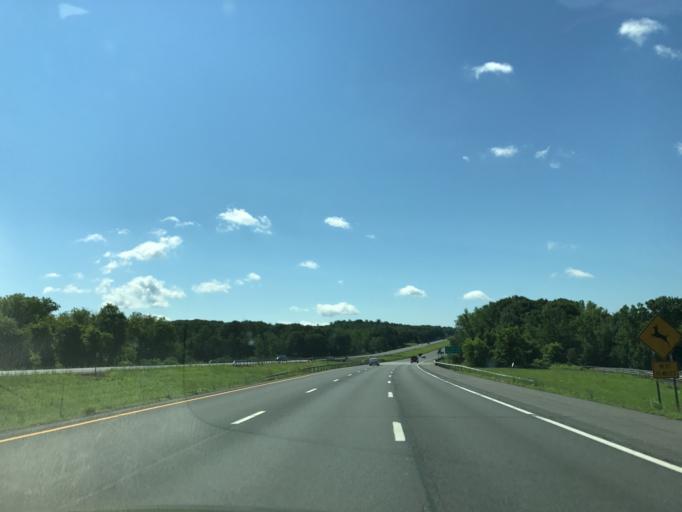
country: US
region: New York
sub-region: Rensselaer County
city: East Greenbush
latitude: 42.6222
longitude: -73.6932
